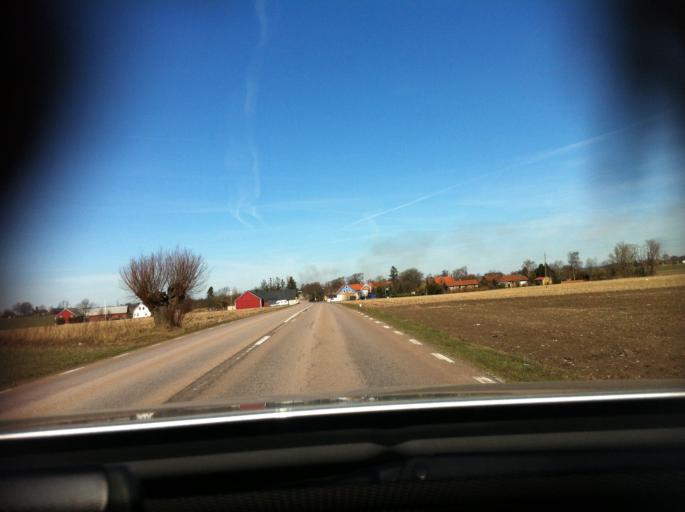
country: SE
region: Skane
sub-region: Landskrona
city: Asmundtorp
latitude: 55.9519
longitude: 12.9467
